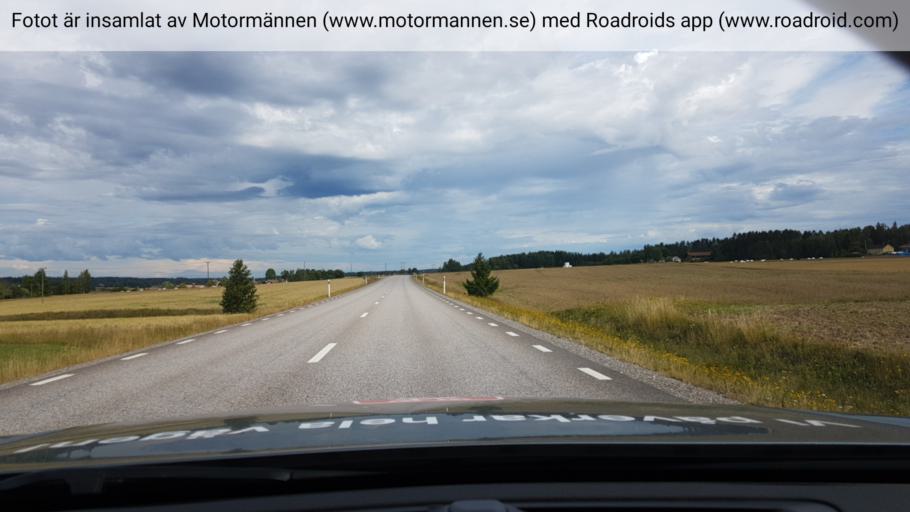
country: SE
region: Uppsala
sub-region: Heby Kommun
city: Heby
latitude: 59.9150
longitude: 16.8871
